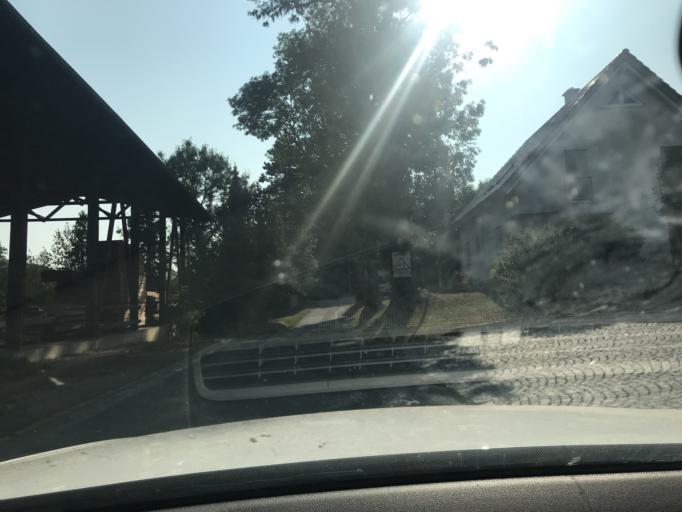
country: DE
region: Bavaria
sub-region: Upper Franconia
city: Pegnitz
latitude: 49.7508
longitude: 11.5455
